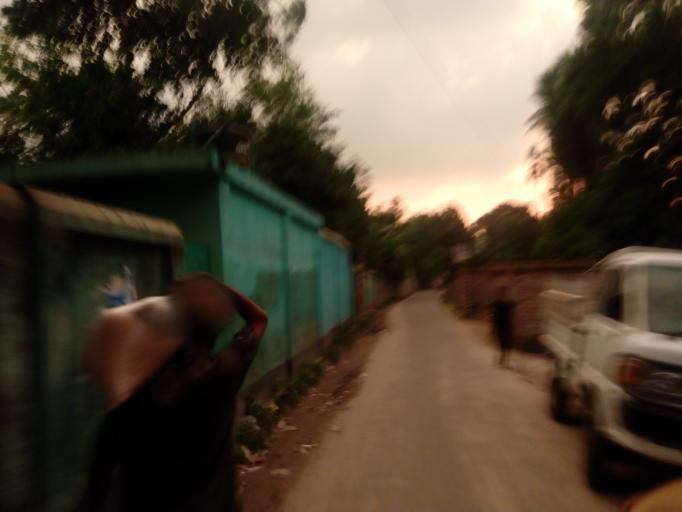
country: BD
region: Rajshahi
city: Sirajganj
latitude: 24.3028
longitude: 89.6948
